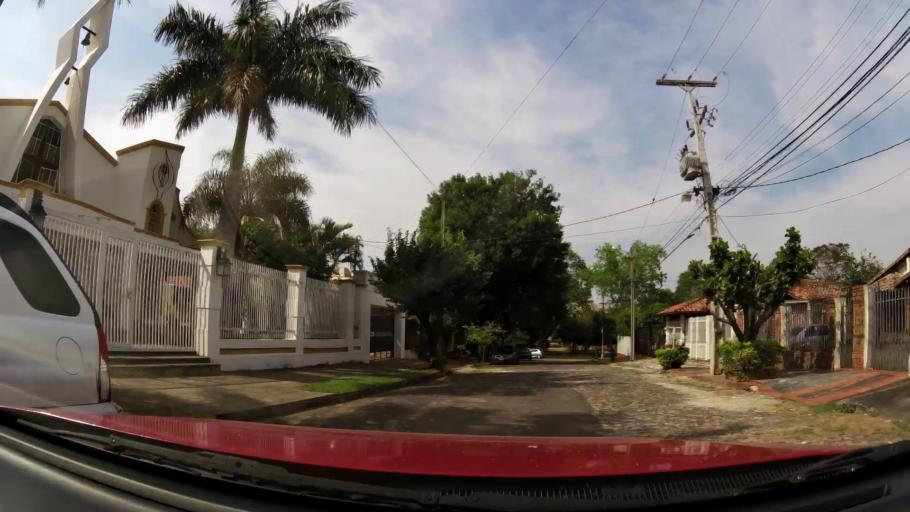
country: PY
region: Asuncion
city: Asuncion
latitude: -25.2629
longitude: -57.5643
